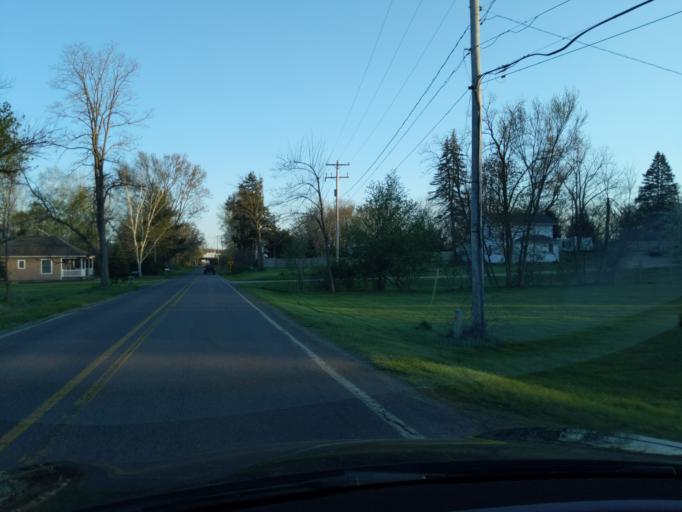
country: US
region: Michigan
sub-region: Jackson County
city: Jackson
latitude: 42.2579
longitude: -84.4833
